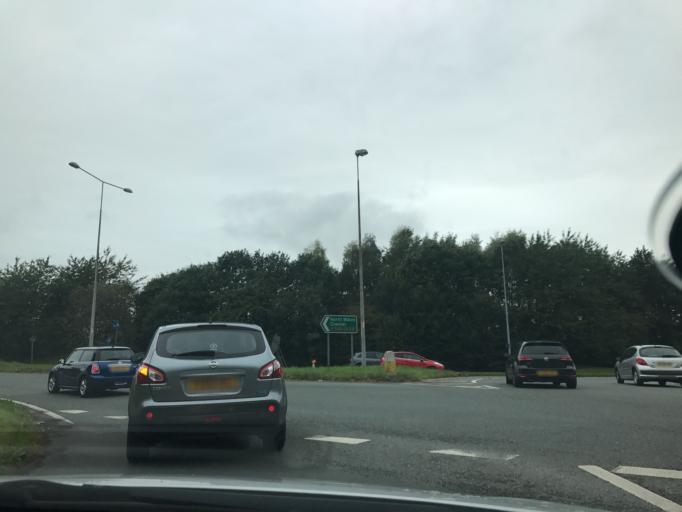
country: GB
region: England
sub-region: Cheshire West and Chester
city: Northwich
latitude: 53.2385
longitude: -2.5131
